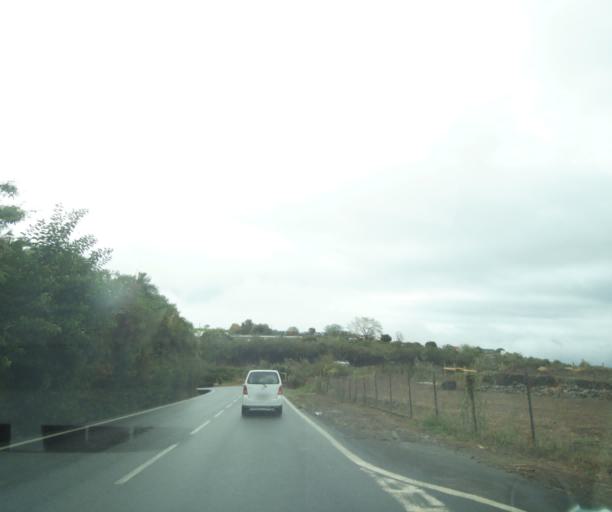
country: RE
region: Reunion
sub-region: Reunion
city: Saint-Paul
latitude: -21.0344
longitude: 55.2813
